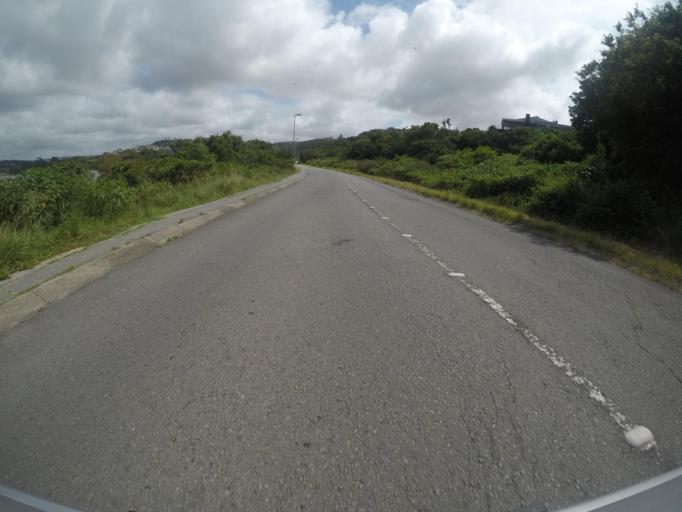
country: ZA
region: Eastern Cape
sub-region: Buffalo City Metropolitan Municipality
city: East London
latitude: -32.9793
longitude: 27.9336
